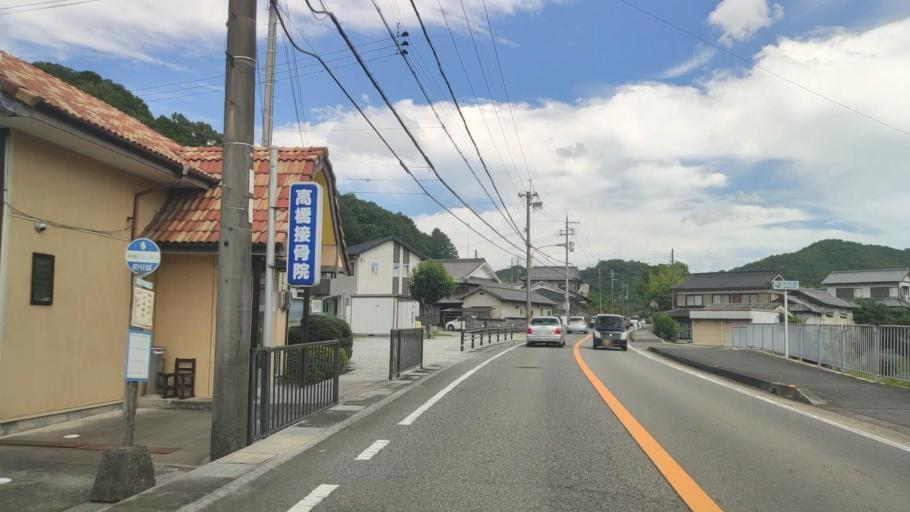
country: JP
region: Hyogo
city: Nishiwaki
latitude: 35.0190
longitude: 134.9503
